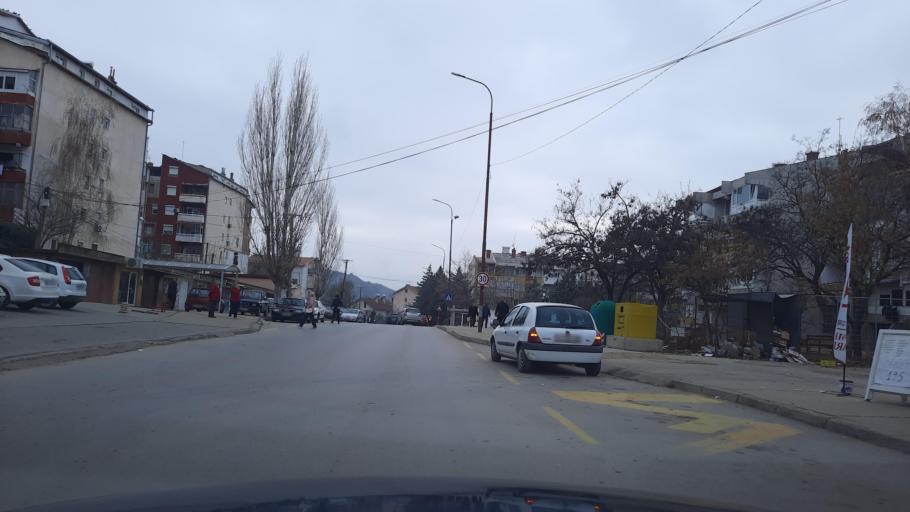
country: MK
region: Stip
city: Shtip
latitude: 41.7494
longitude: 22.1993
